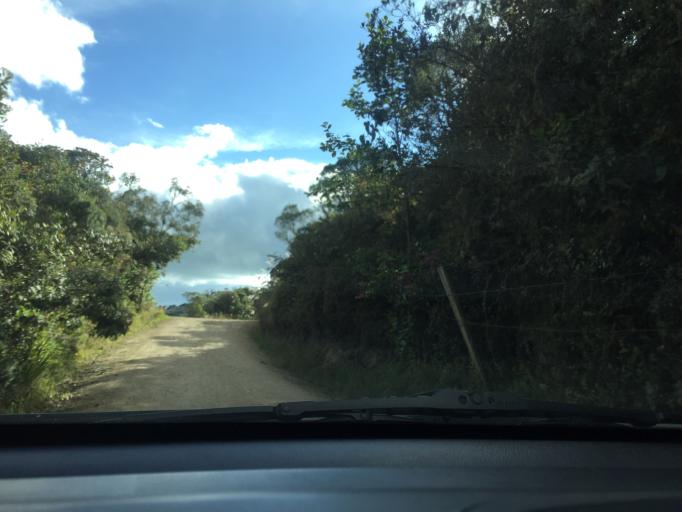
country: CO
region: Cundinamarca
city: Sopo
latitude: 4.9211
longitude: -73.9085
